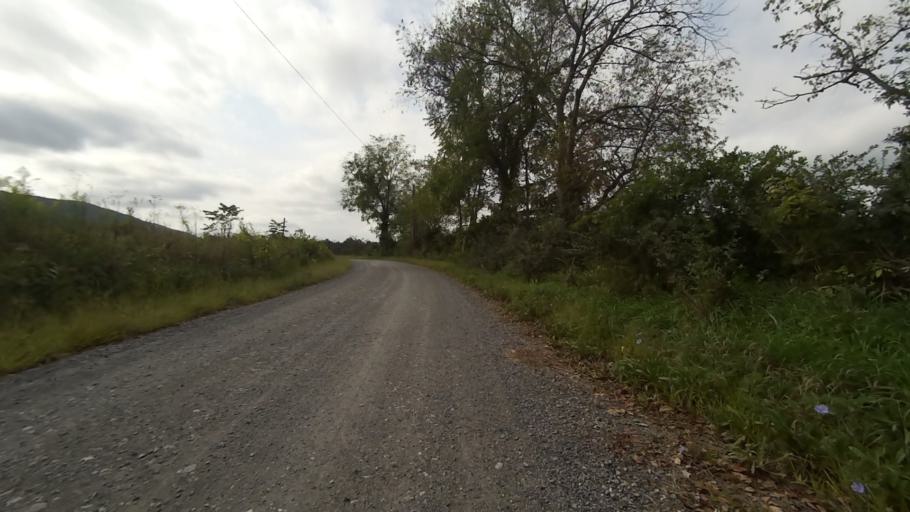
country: US
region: Pennsylvania
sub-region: Blair County
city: Williamsburg
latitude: 40.5565
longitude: -78.1562
